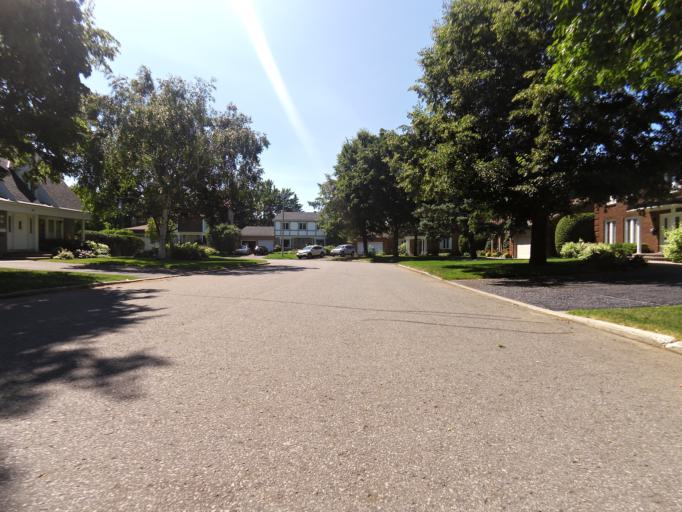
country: CA
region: Ontario
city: Ottawa
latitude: 45.3453
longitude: -75.6719
